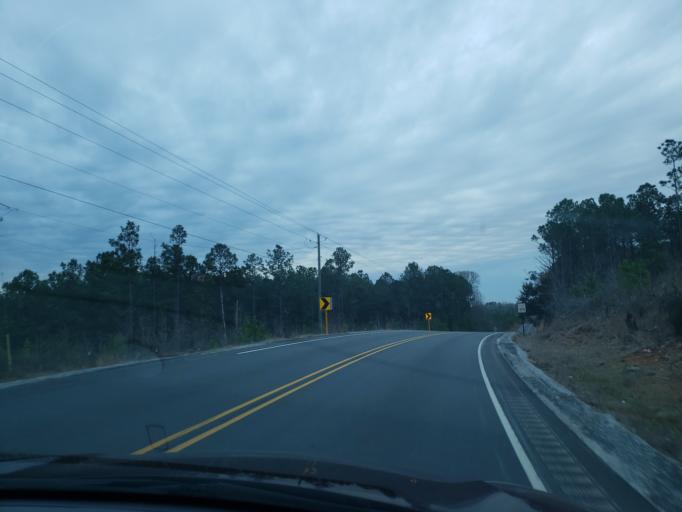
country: US
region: Alabama
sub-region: Randolph County
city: Roanoke
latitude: 33.0463
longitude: -85.3451
